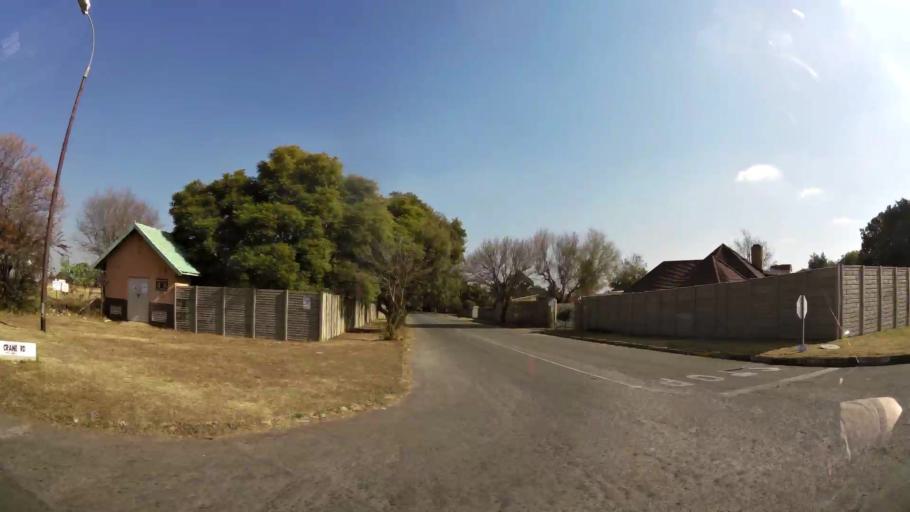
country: ZA
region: Gauteng
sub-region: West Rand District Municipality
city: Randfontein
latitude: -26.1603
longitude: 27.7039
